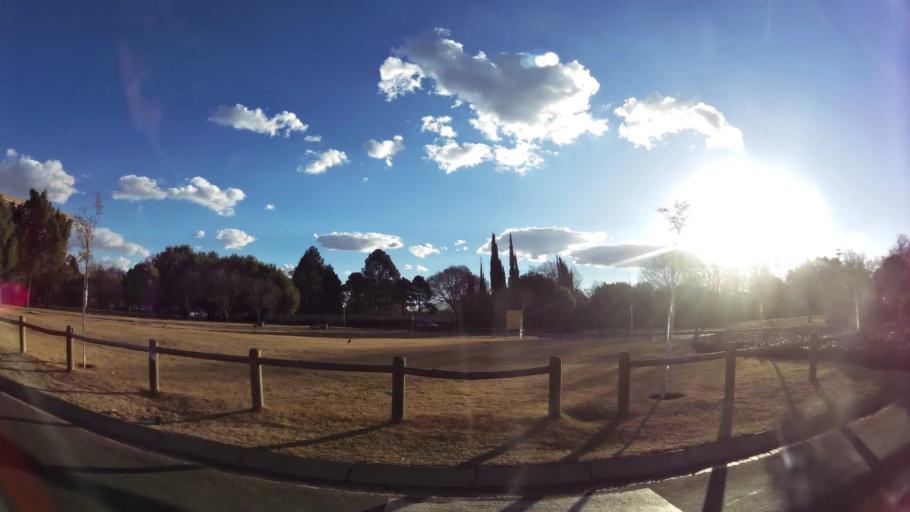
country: ZA
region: North-West
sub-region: Dr Kenneth Kaunda District Municipality
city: Potchefstroom
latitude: -26.6958
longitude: 27.0885
